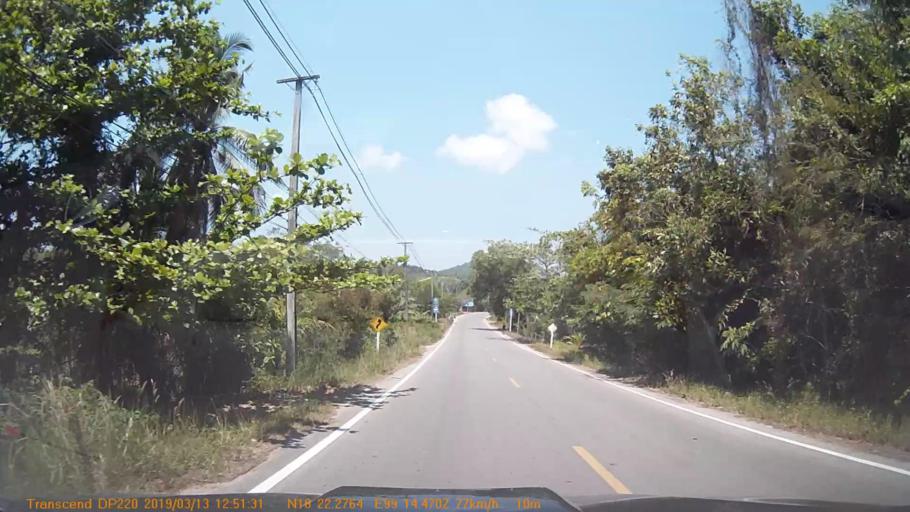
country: TH
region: Chumphon
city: Chumphon
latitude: 10.3716
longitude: 99.2412
